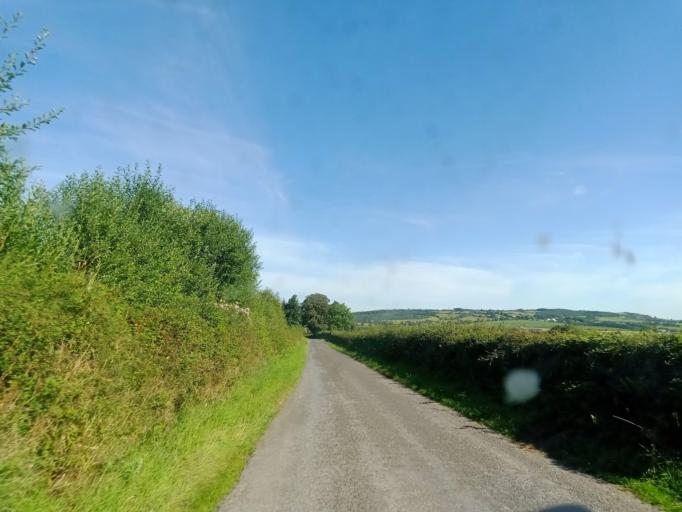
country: IE
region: Leinster
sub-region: Kilkenny
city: Ballyragget
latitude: 52.7943
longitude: -7.4245
